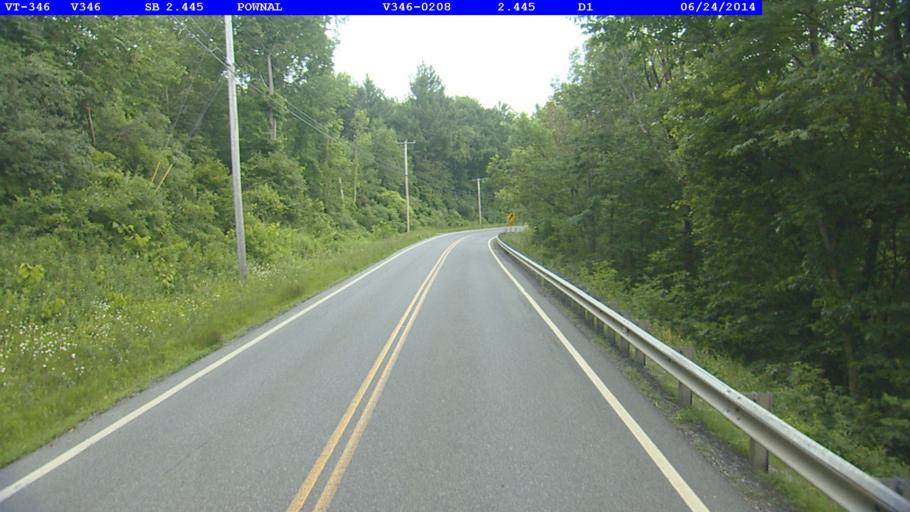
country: US
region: Massachusetts
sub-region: Berkshire County
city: Williamstown
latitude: 42.7924
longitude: -73.2563
